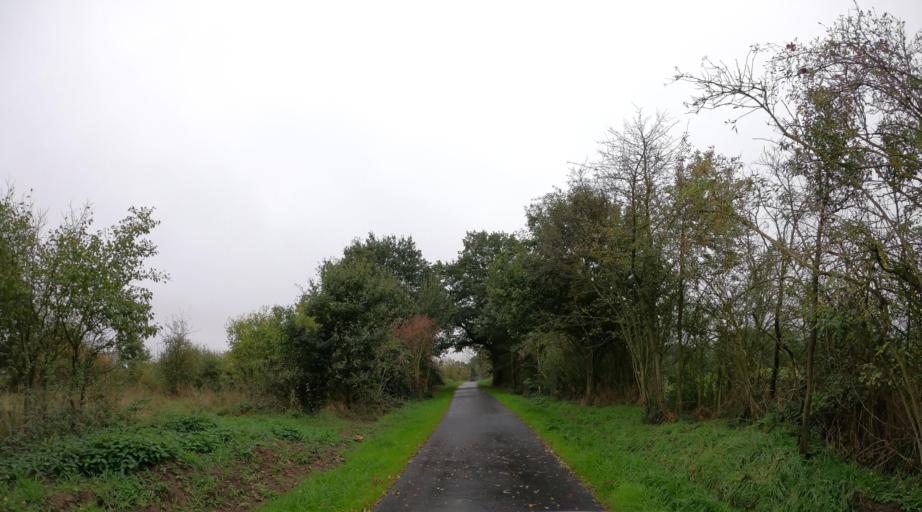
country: PL
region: West Pomeranian Voivodeship
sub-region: Powiat mysliborski
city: Mysliborz
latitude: 52.9172
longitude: 14.7426
